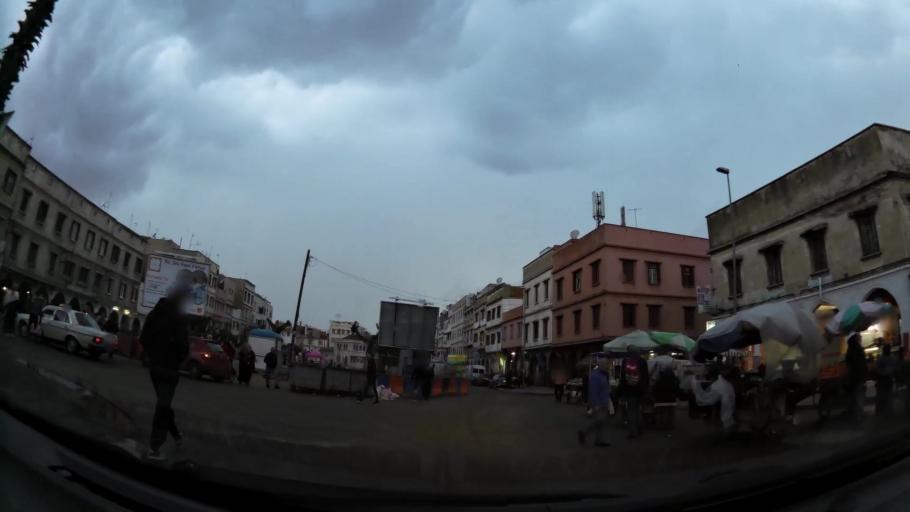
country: MA
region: Grand Casablanca
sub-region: Casablanca
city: Casablanca
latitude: 33.5689
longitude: -7.6007
